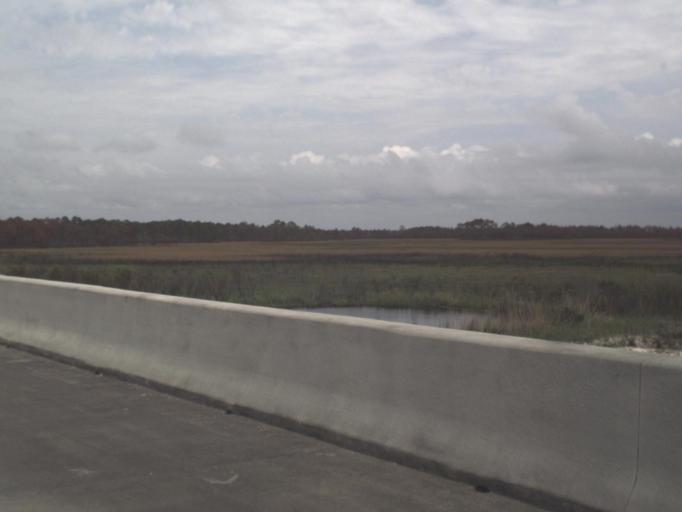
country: US
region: Florida
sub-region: Santa Rosa County
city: Oriole Beach
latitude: 30.4435
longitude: -87.1005
